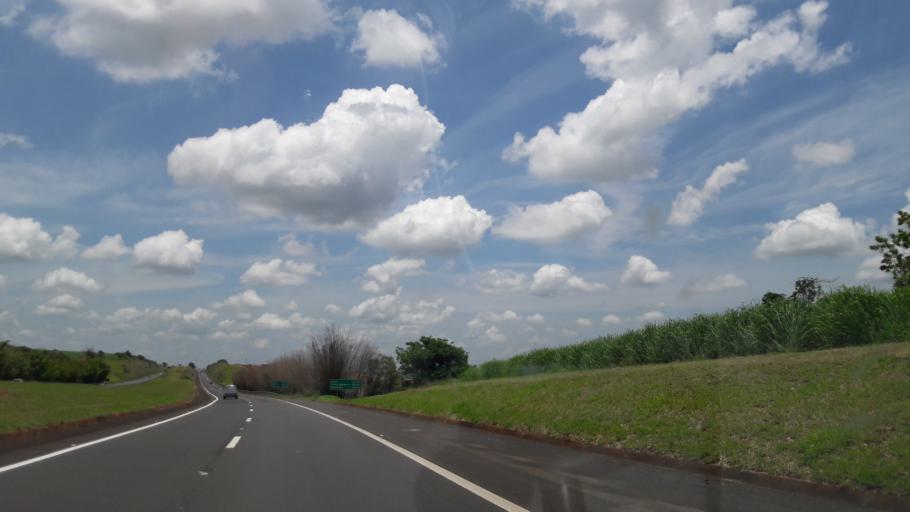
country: BR
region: Sao Paulo
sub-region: Avare
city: Avare
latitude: -22.9544
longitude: -48.8275
